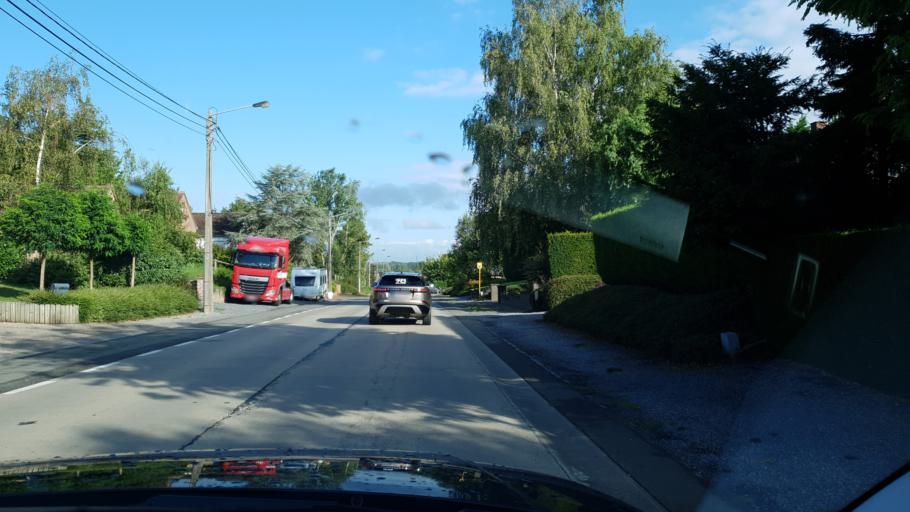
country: BE
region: Wallonia
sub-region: Province du Hainaut
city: Pecq
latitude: 50.6500
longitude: 3.3643
